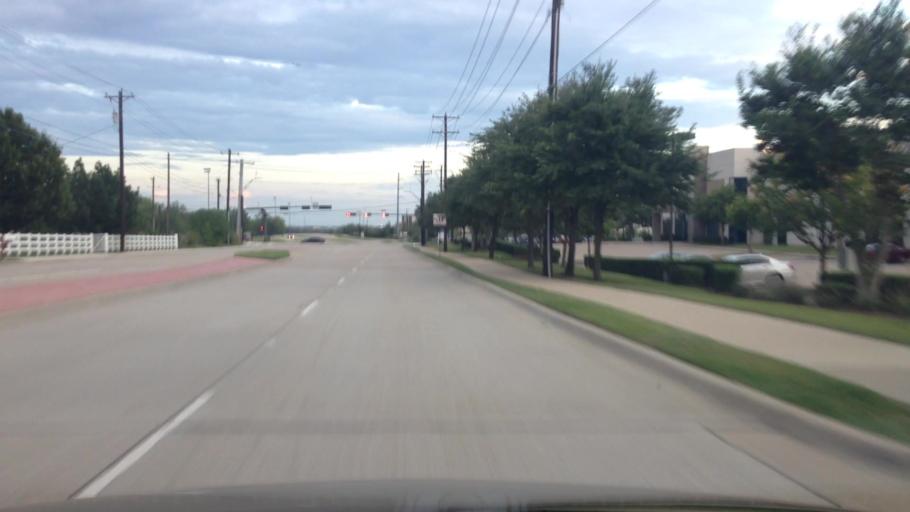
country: US
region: Texas
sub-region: Denton County
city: Flower Mound
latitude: 32.9986
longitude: -97.0483
